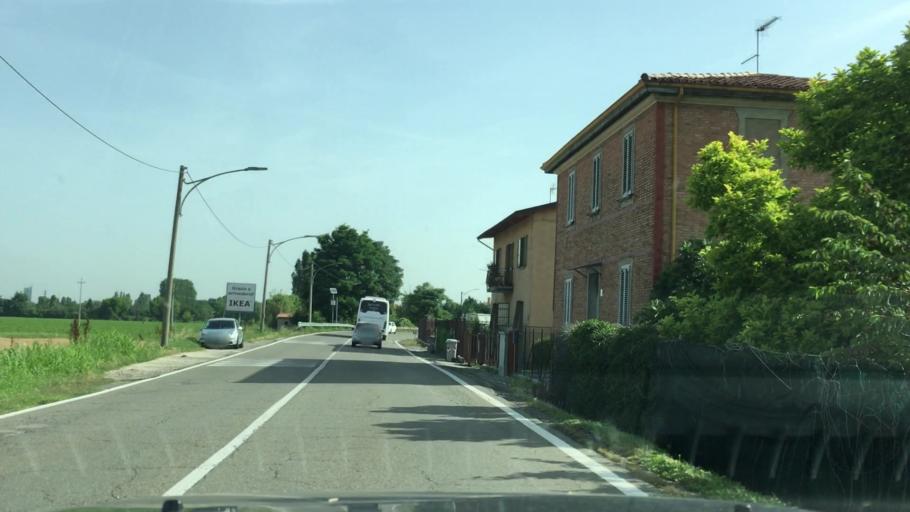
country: IT
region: Emilia-Romagna
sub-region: Provincia di Bologna
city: Progresso
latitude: 44.5425
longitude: 11.3728
